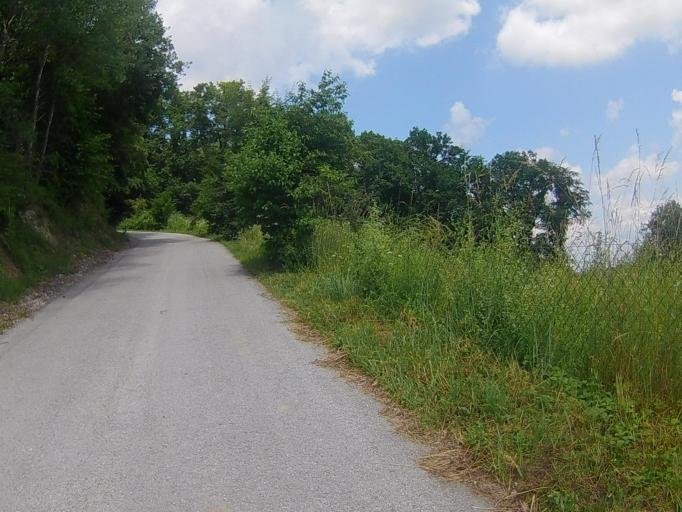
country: SI
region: Kungota
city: Zgornja Kungota
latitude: 46.6192
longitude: 15.6272
